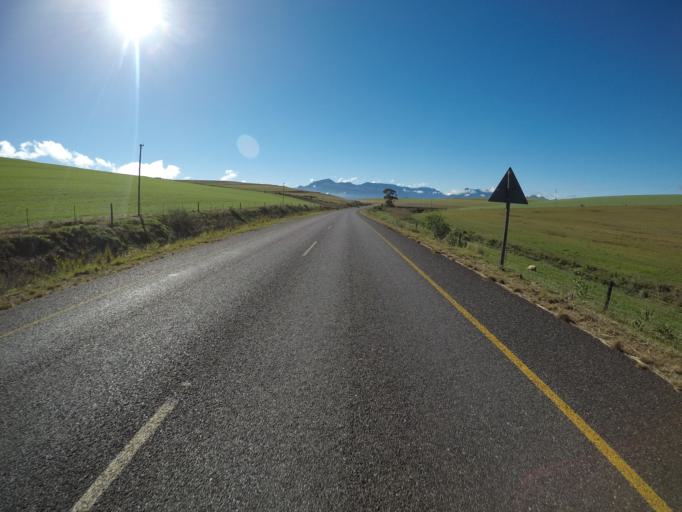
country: ZA
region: Western Cape
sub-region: Overberg District Municipality
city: Caledon
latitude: -34.1361
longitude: 19.5084
